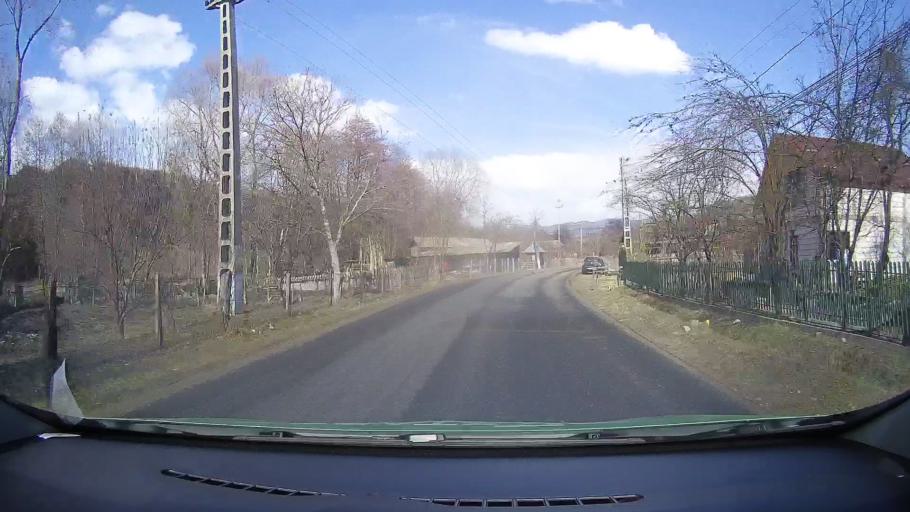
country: RO
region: Dambovita
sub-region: Comuna Runcu
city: Badeni
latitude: 45.1568
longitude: 25.3985
